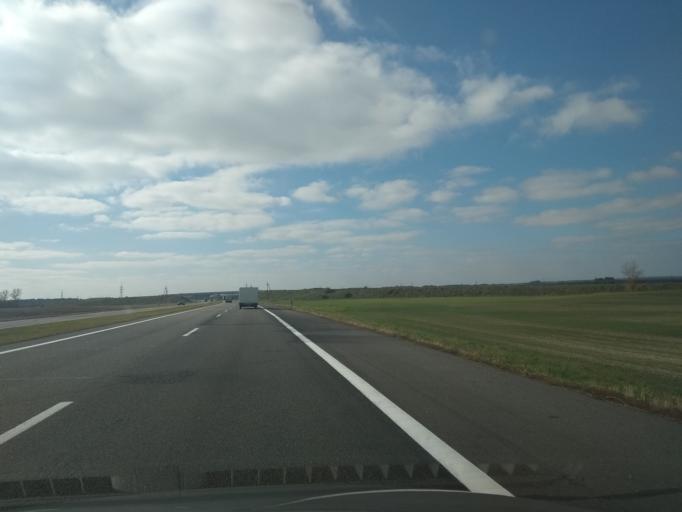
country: BY
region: Brest
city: Haradzishcha
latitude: 53.2376
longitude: 26.1826
